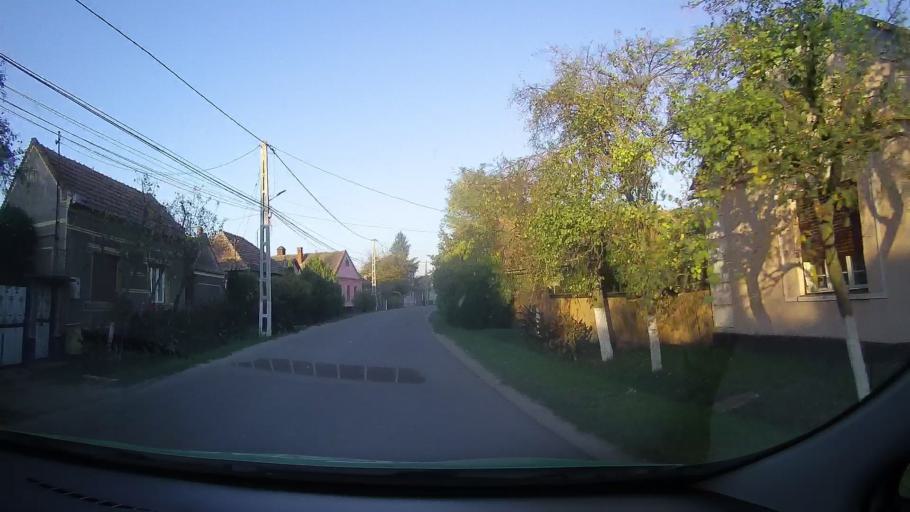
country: RO
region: Bihor
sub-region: Comuna Salard
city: Salard
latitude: 47.2281
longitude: 22.0295
